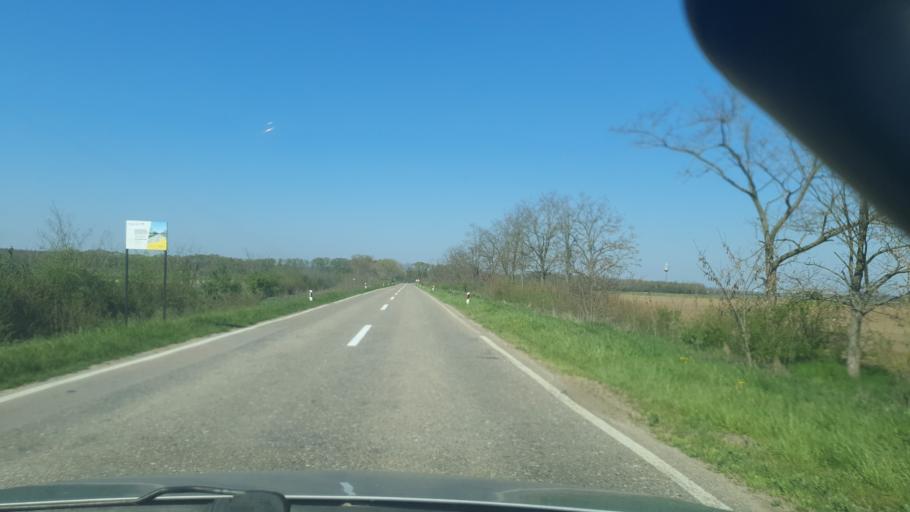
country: RS
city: Kolut
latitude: 45.8394
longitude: 18.9709
